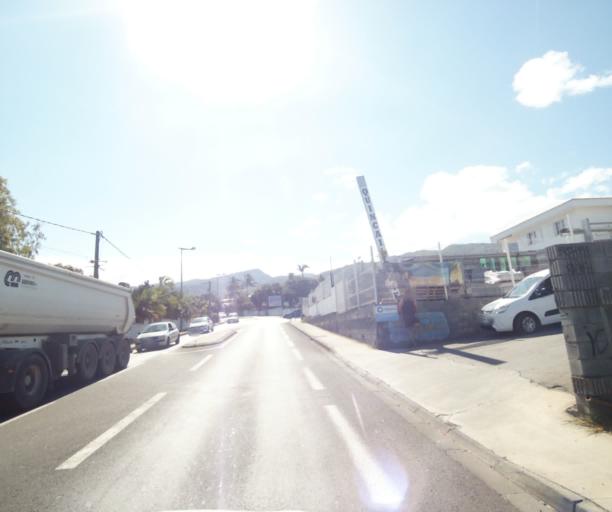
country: RE
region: Reunion
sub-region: Reunion
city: La Possession
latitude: -20.9781
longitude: 55.3235
